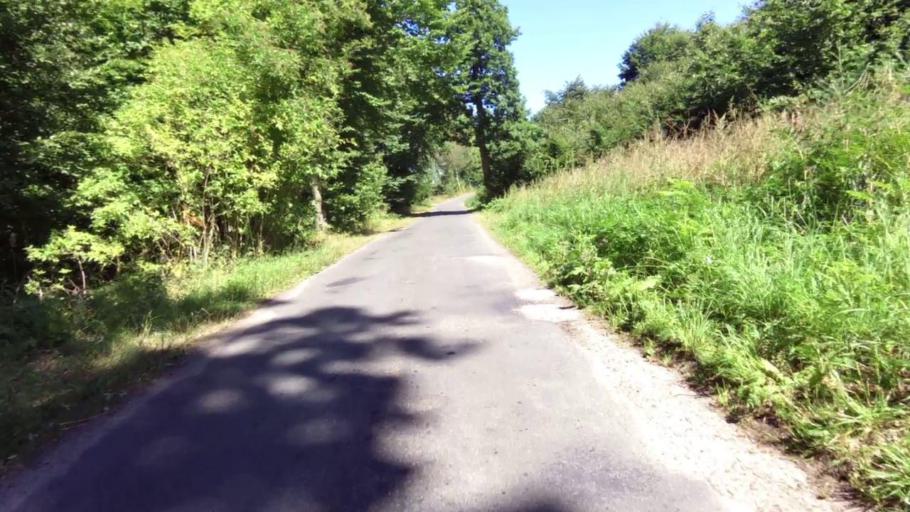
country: PL
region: West Pomeranian Voivodeship
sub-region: Powiat drawski
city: Czaplinek
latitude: 53.5204
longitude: 16.1977
